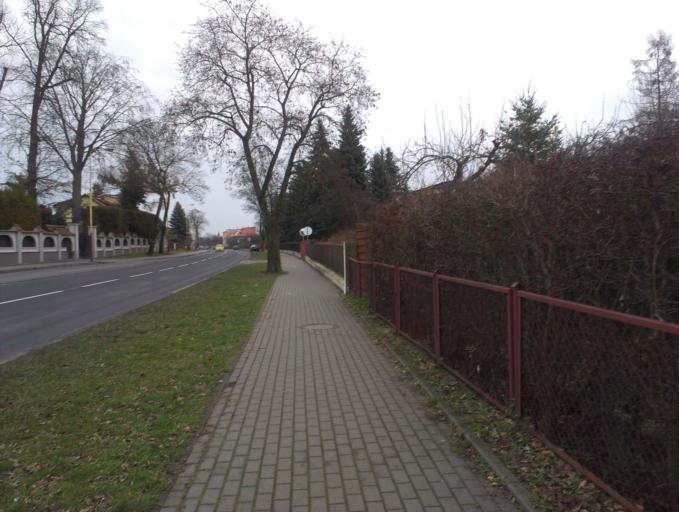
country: PL
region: West Pomeranian Voivodeship
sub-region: Powiat szczecinecki
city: Szczecinek
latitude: 53.6903
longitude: 16.6945
